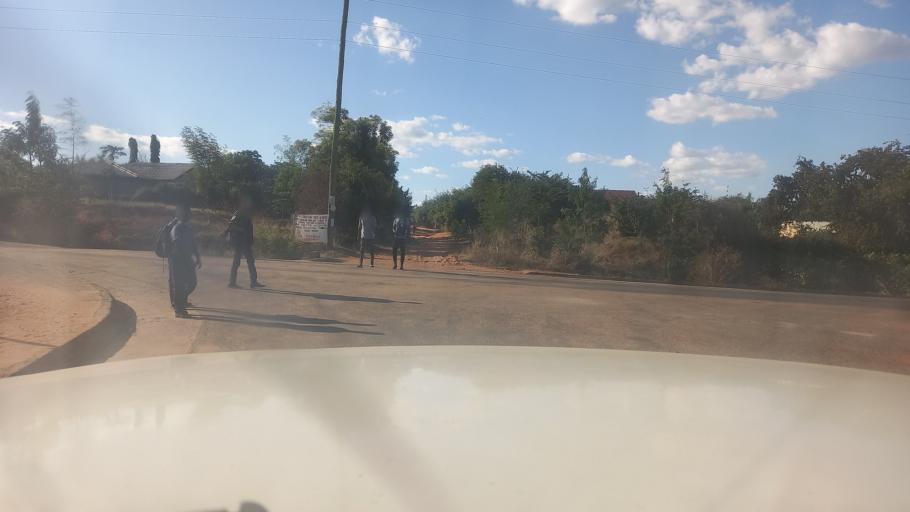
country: ZM
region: Southern
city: Livingstone
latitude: -17.8303
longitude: 25.8664
